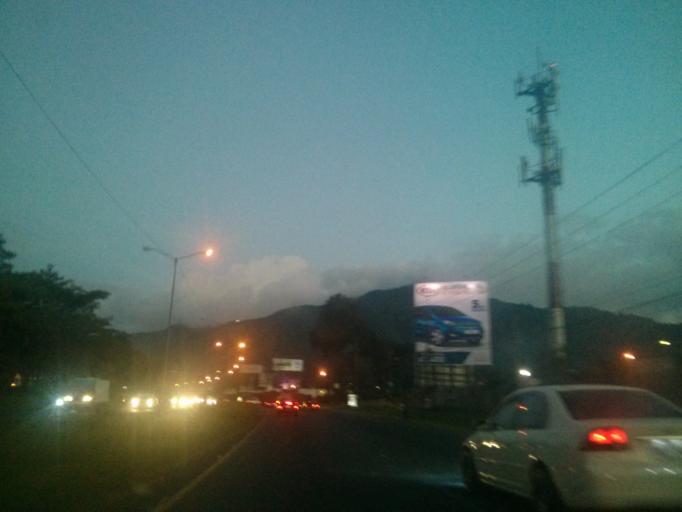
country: CR
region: Cartago
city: San Diego
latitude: 9.9018
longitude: -84.0065
